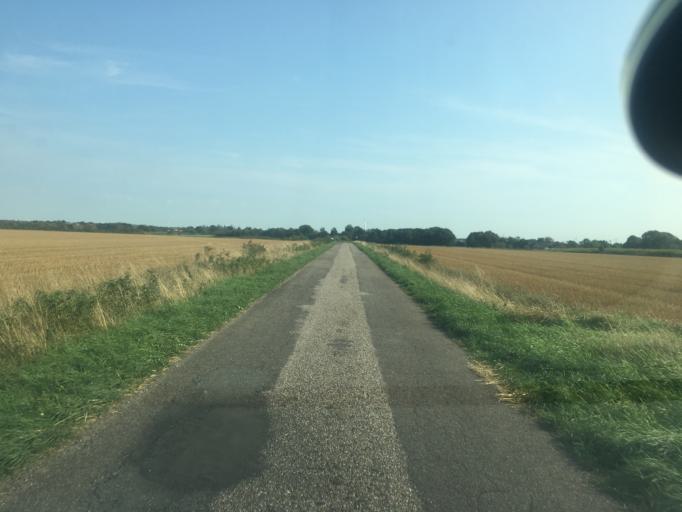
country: DK
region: South Denmark
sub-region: Tonder Kommune
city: Tonder
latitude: 54.9641
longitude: 8.8991
